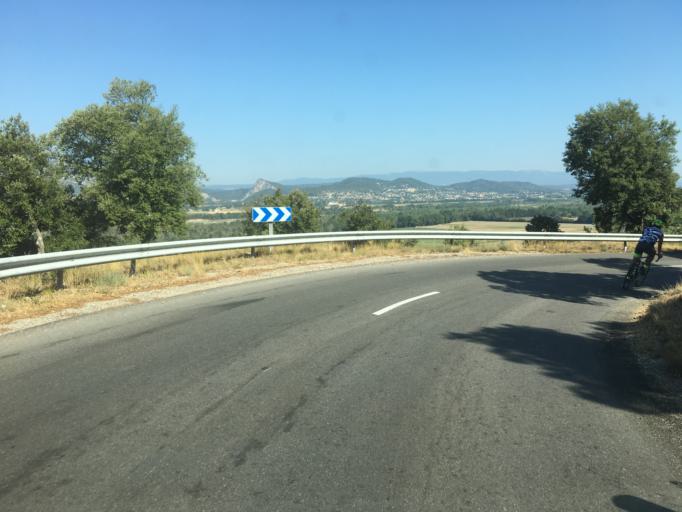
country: FR
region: Provence-Alpes-Cote d'Azur
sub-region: Departement des Alpes-de-Haute-Provence
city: Volx
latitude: 43.8471
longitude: 5.8765
